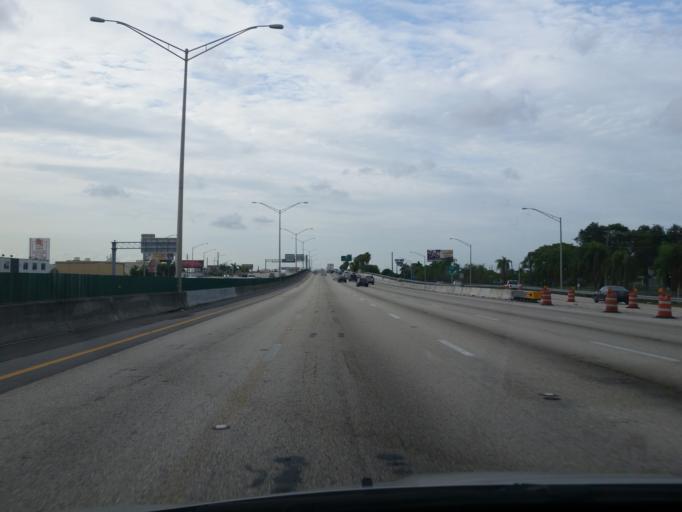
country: US
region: Florida
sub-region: Broward County
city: Pembroke Park
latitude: 25.9912
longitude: -80.1658
